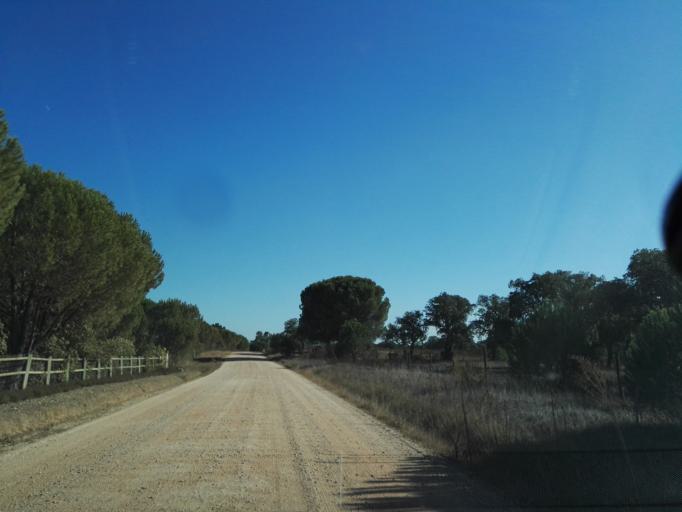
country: PT
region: Santarem
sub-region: Benavente
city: Poceirao
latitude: 38.8793
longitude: -8.7417
